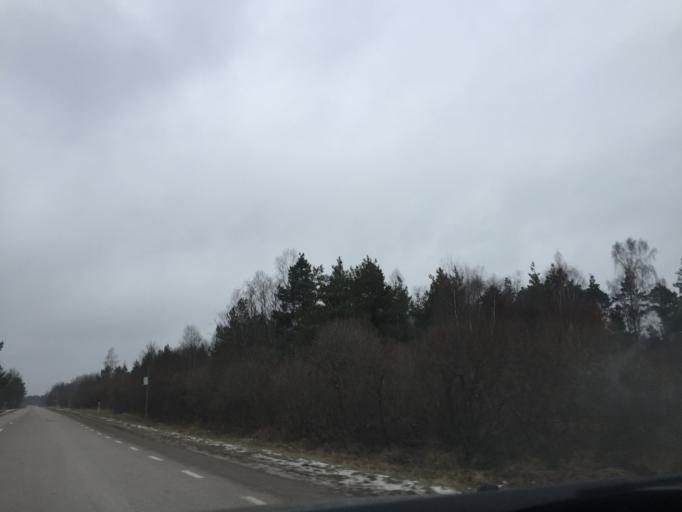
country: EE
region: Saare
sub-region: Kuressaare linn
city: Kuressaare
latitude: 58.2792
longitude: 22.4345
